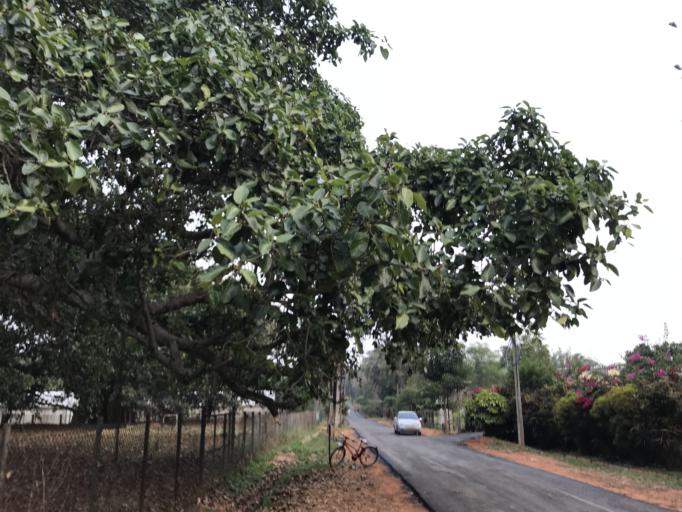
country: IN
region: Karnataka
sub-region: Bangalore Urban
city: Yelahanka
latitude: 13.0819
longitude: 77.5669
